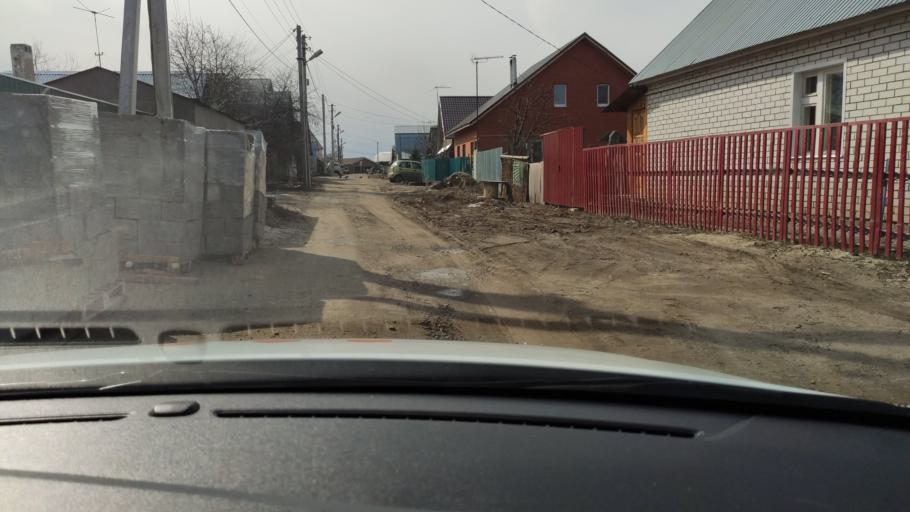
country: RU
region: Tatarstan
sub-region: Gorod Kazan'
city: Kazan
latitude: 55.7268
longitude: 49.1426
